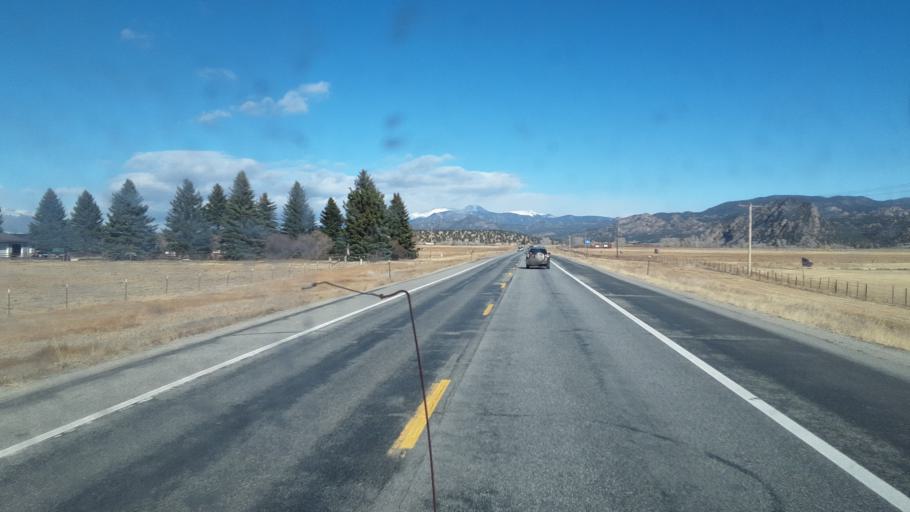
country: US
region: Colorado
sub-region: Chaffee County
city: Buena Vista
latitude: 38.7291
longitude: -106.0859
